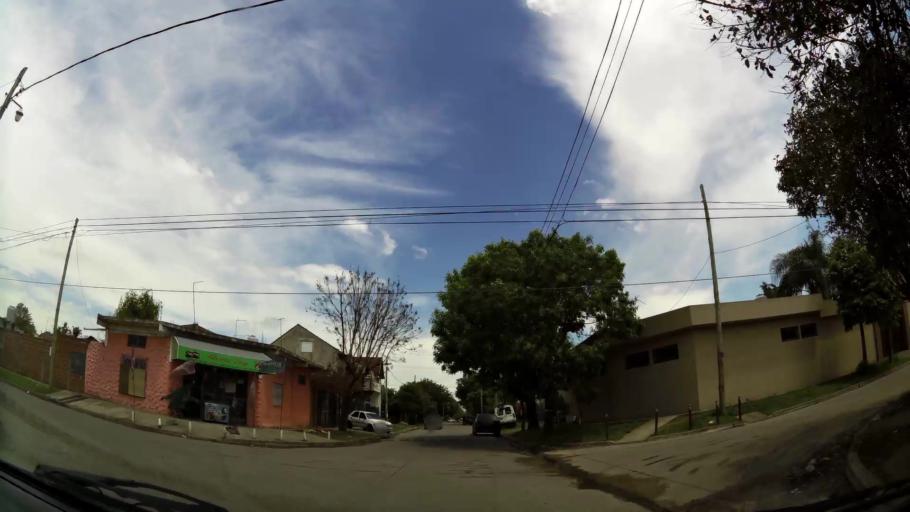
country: AR
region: Buenos Aires
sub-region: Partido de Quilmes
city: Quilmes
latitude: -34.7870
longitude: -58.2611
